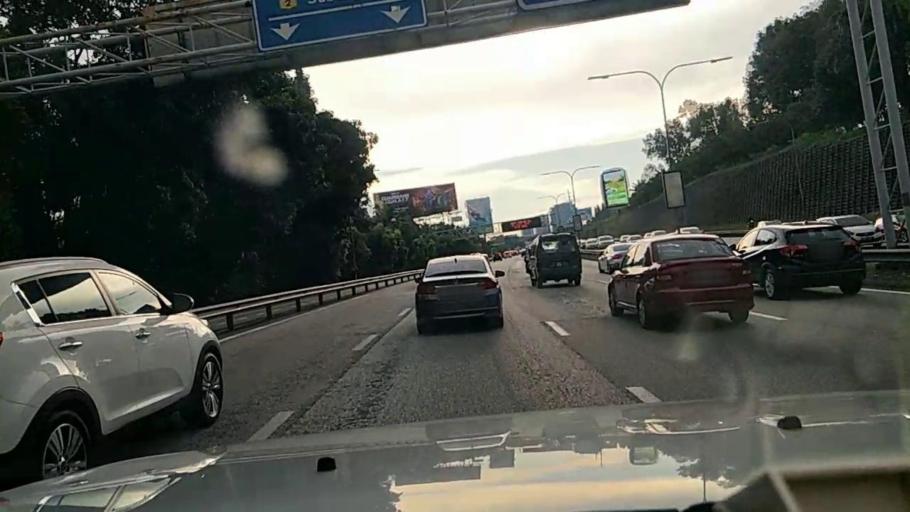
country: MY
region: Selangor
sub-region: Petaling
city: Petaling Jaya
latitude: 3.0831
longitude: 101.6012
